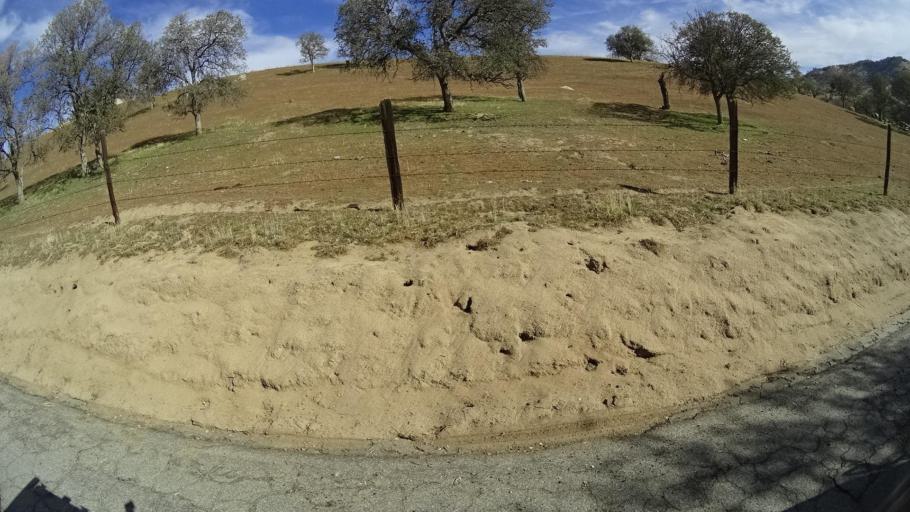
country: US
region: California
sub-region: Kern County
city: Oildale
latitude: 35.5653
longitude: -118.7966
